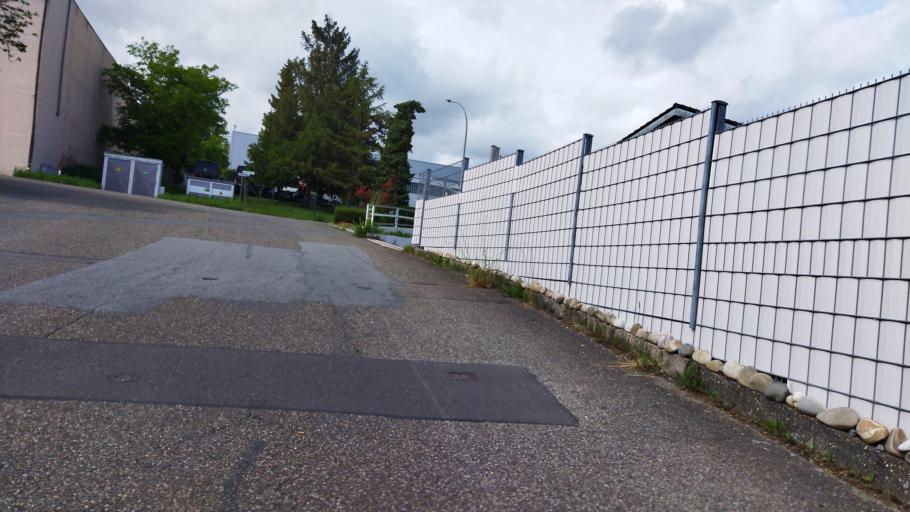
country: DE
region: Baden-Wuerttemberg
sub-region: Regierungsbezirk Stuttgart
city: Leingarten
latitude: 49.1485
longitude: 9.1294
